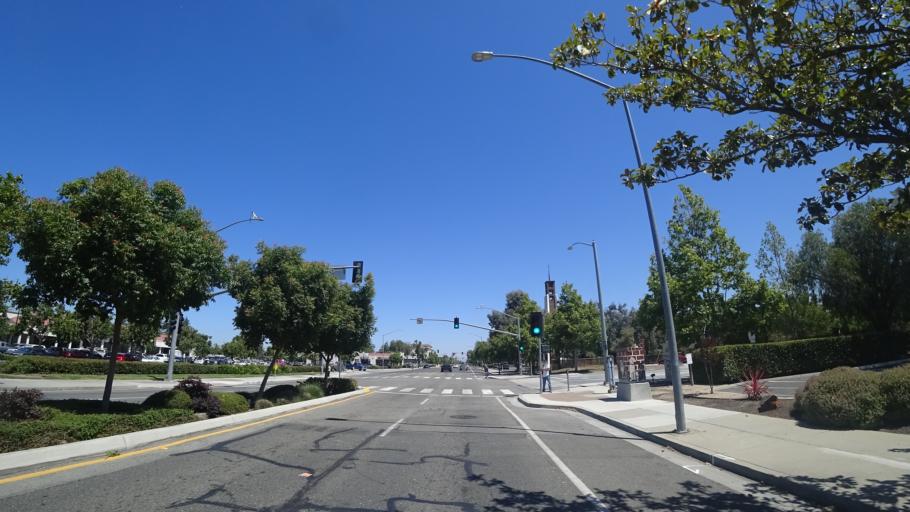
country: US
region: California
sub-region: Santa Clara County
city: Campbell
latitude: 37.2791
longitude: -121.9497
